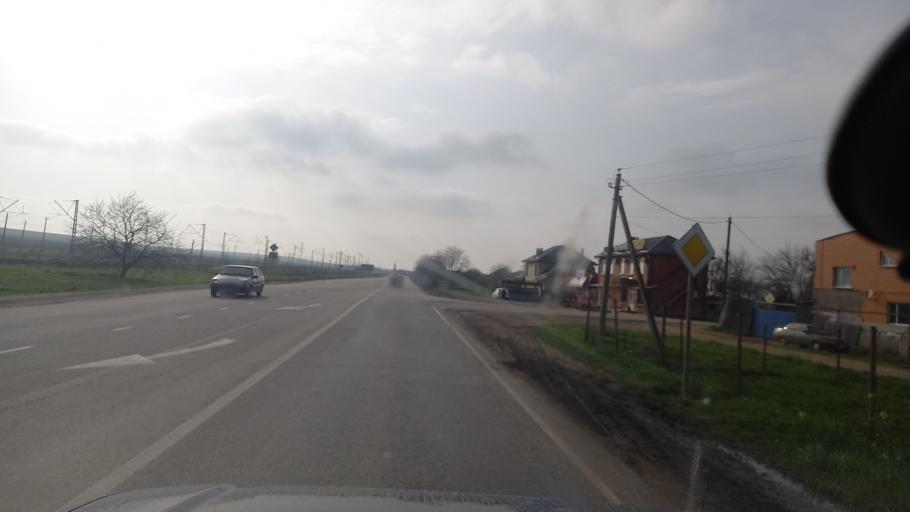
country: RU
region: Krasnodarskiy
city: Varenikovskaya
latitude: 45.1124
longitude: 37.6310
